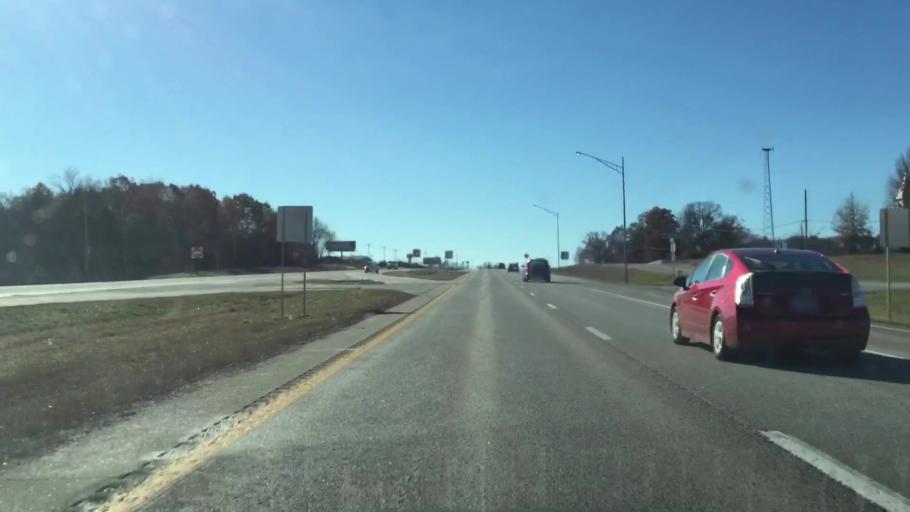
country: US
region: Missouri
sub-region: Cole County
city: Wardsville
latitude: 38.4462
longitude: -92.3028
